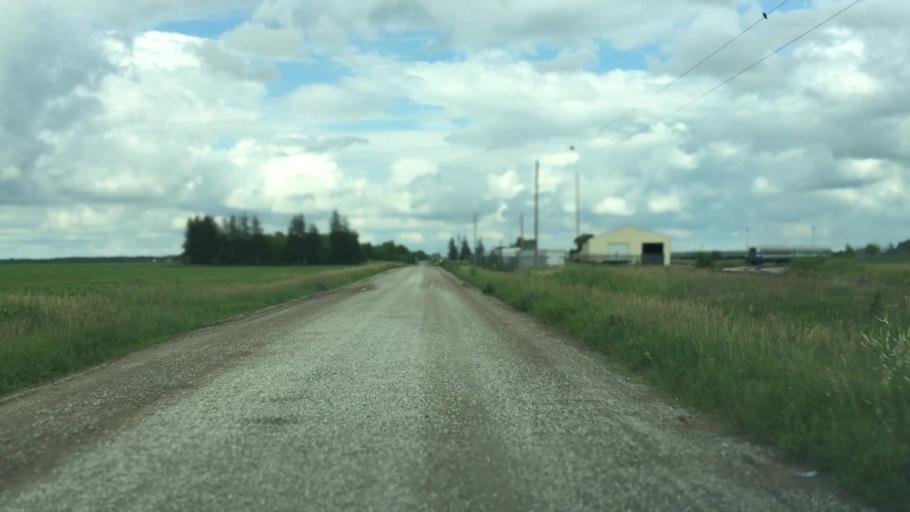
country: US
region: Iowa
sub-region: Jasper County
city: Newton
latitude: 41.7353
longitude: -93.0164
